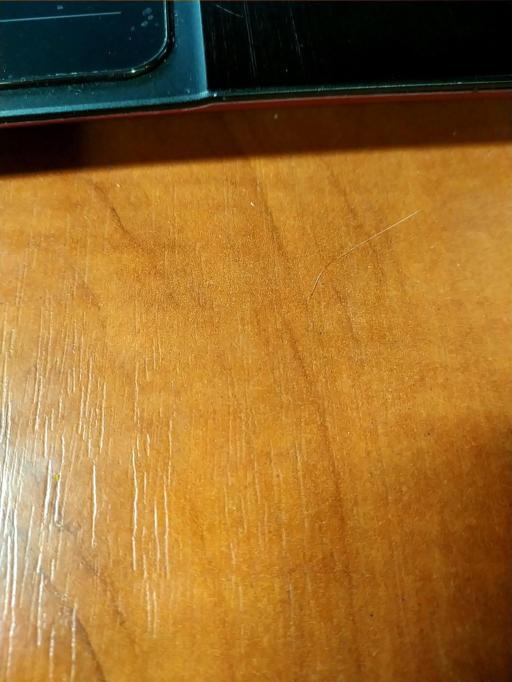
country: RU
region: Smolensk
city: Ozernyy
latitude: 55.4358
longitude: 32.7206
